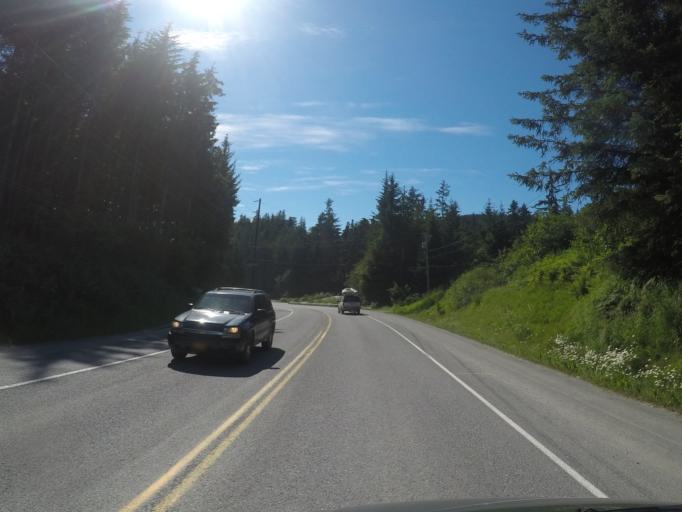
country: US
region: Alaska
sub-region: Juneau City and Borough
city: Juneau
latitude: 58.3832
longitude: -134.6658
